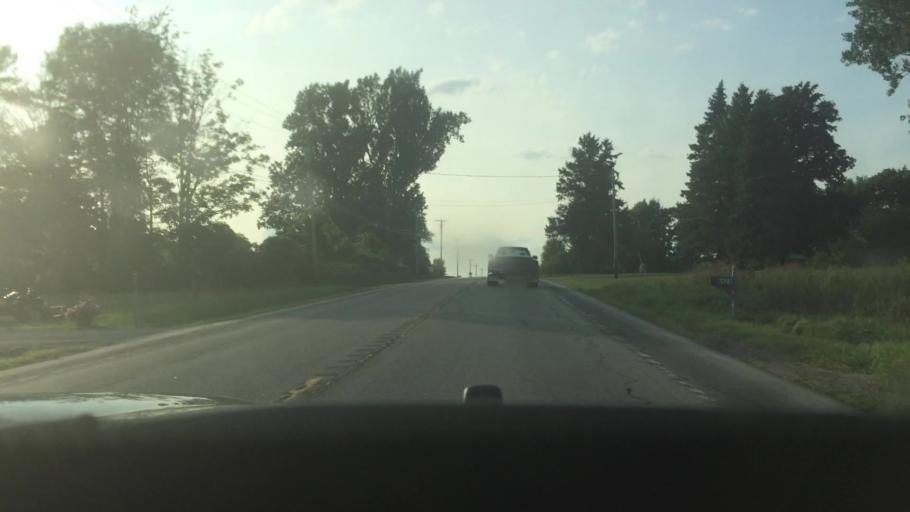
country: US
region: New York
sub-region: St. Lawrence County
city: Ogdensburg
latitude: 44.6776
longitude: -75.4388
